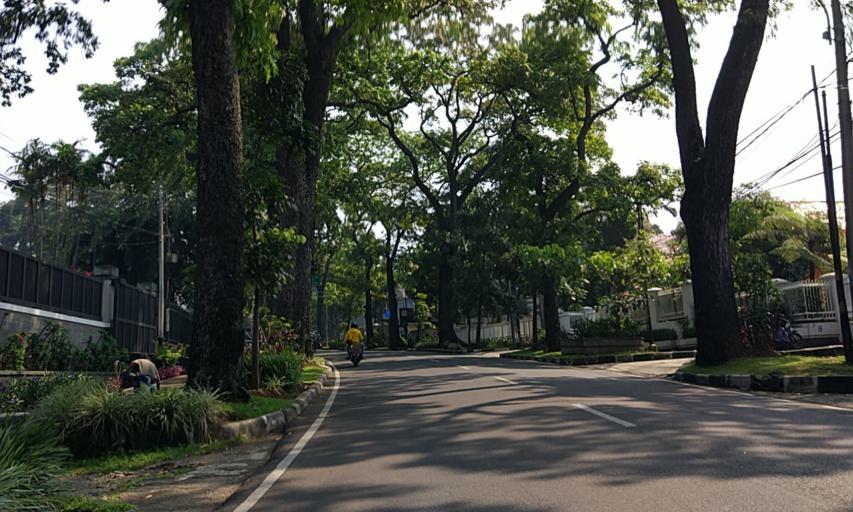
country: ID
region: West Java
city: Bandung
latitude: -6.9037
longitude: 107.6030
